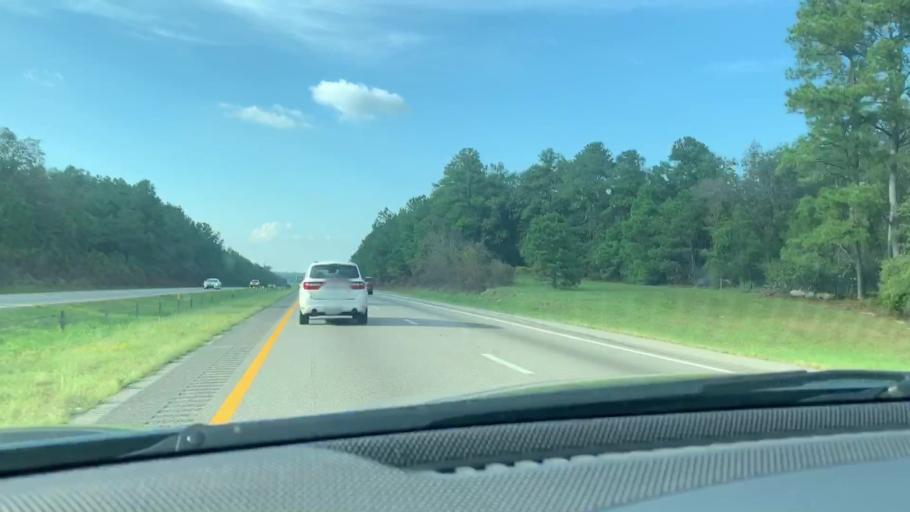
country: US
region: South Carolina
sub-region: Calhoun County
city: Oak Grove
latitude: 33.7390
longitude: -80.9368
